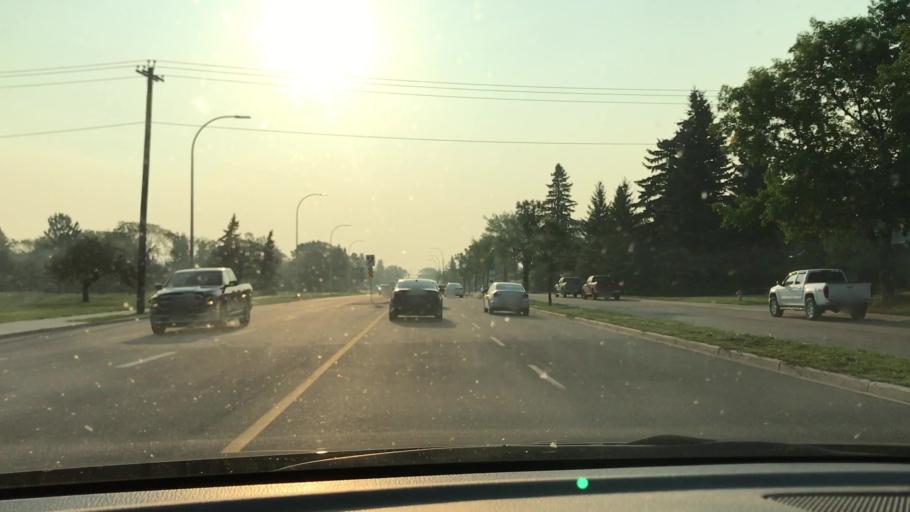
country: CA
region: Alberta
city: Edmonton
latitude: 53.5374
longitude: -113.4492
